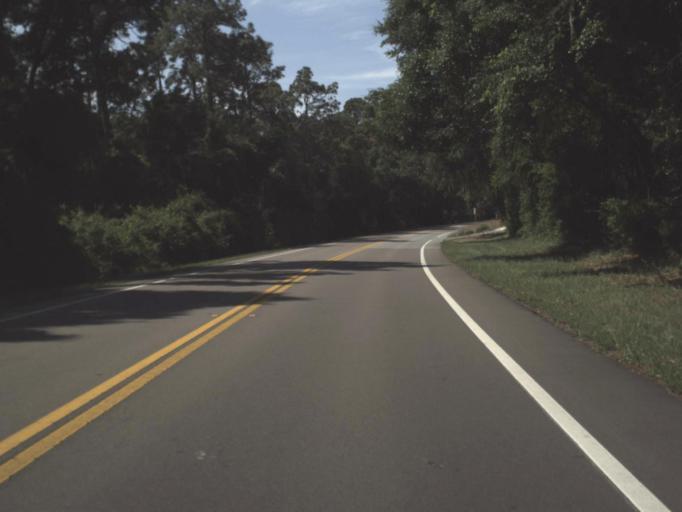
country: US
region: Florida
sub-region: Duval County
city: Atlantic Beach
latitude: 30.4680
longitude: -81.4392
